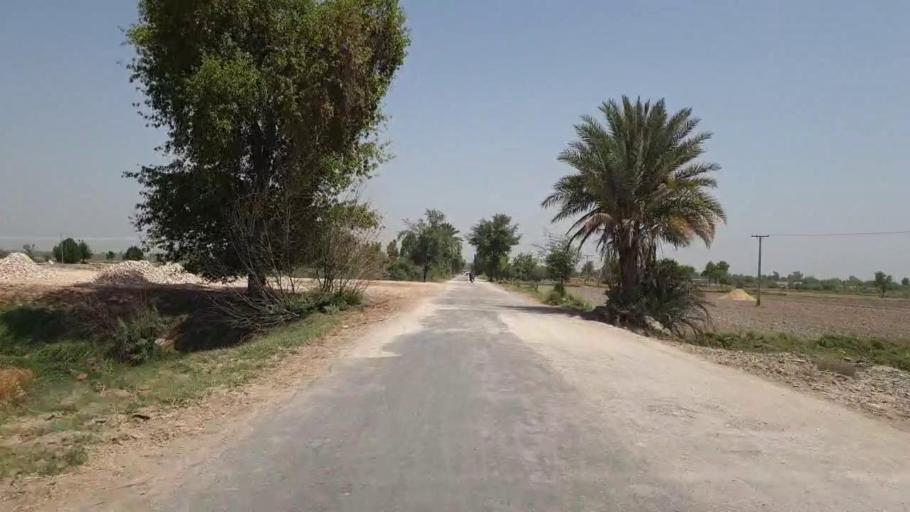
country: PK
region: Sindh
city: Adilpur
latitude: 27.8860
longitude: 69.2880
